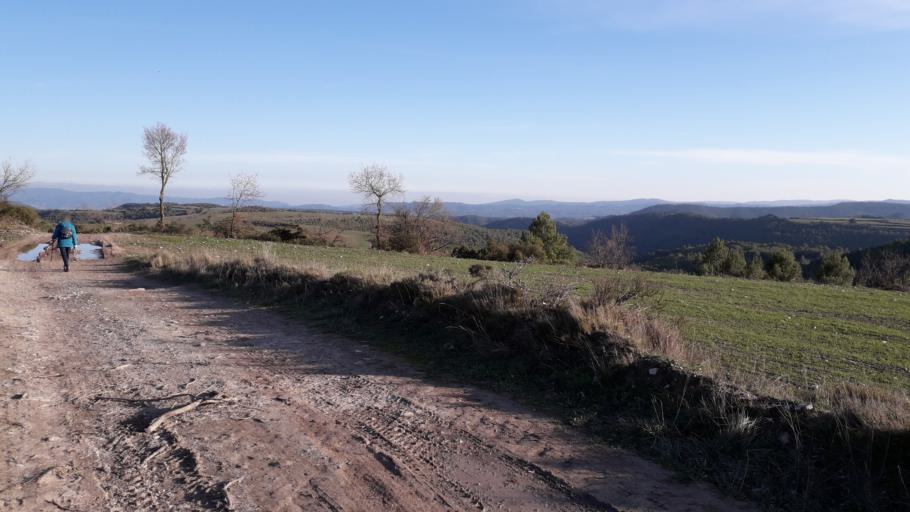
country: ES
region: Catalonia
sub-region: Provincia de Lleida
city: Sant Guim de Freixenet
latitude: 41.6155
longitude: 1.4670
